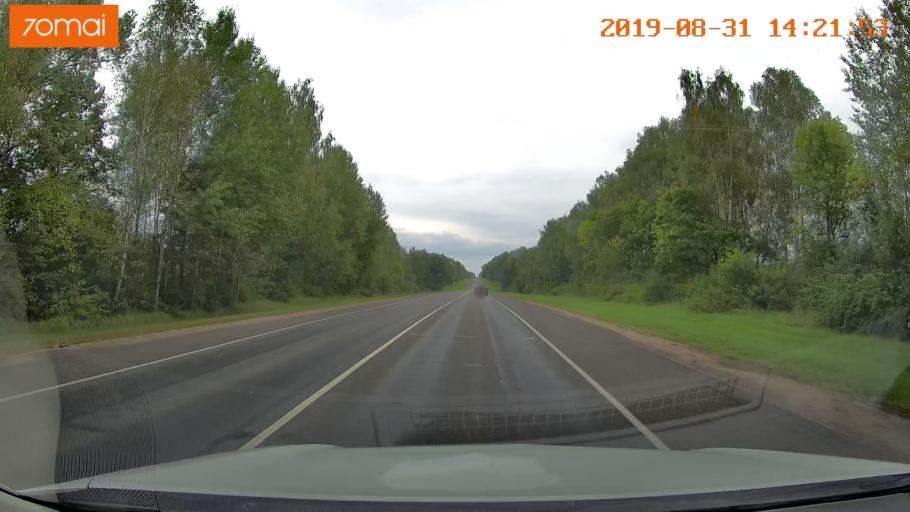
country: RU
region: Smolensk
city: Yekimovichi
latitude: 54.0880
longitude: 33.2059
